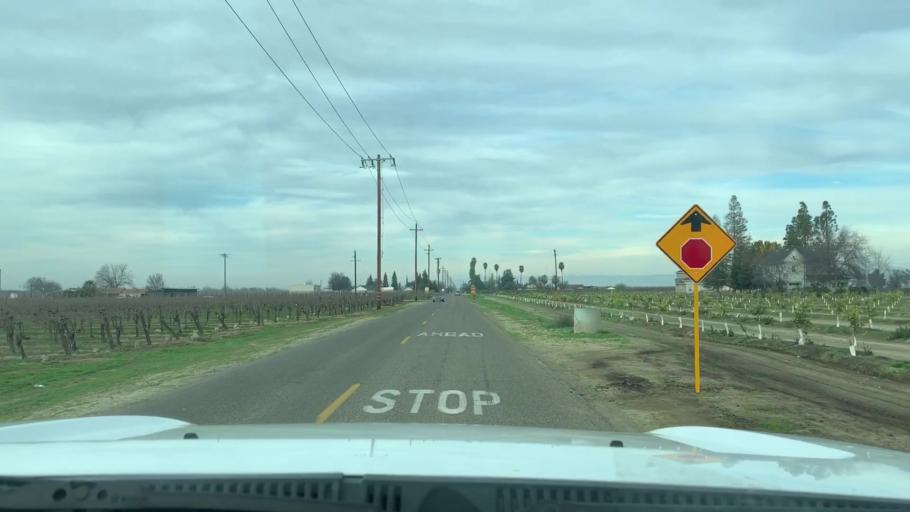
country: US
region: California
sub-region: Fresno County
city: Selma
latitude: 36.5599
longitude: -119.5750
